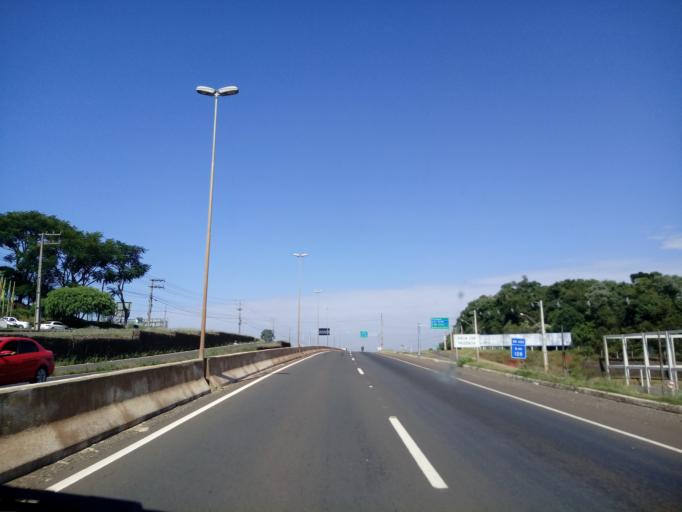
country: BR
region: Santa Catarina
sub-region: Chapeco
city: Chapeco
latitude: -27.0376
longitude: -52.6343
